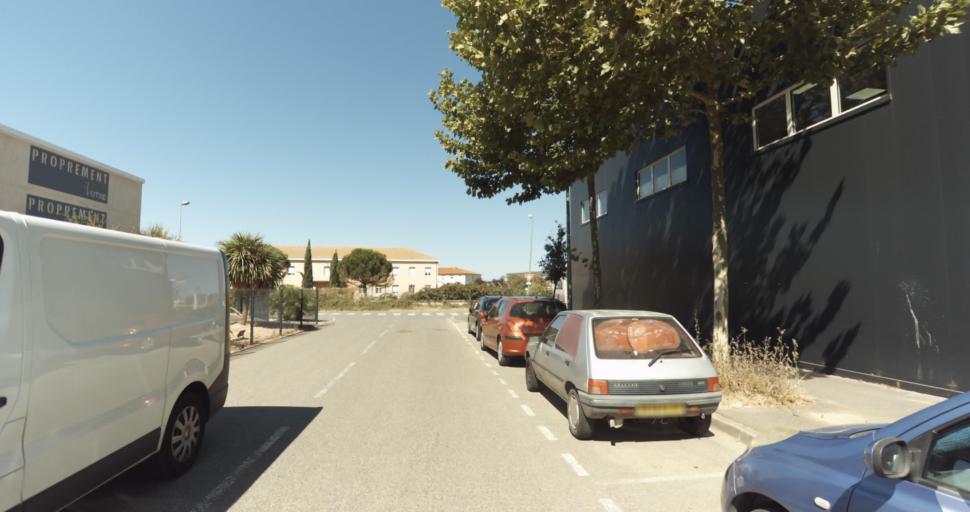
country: FR
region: Midi-Pyrenees
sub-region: Departement de la Haute-Garonne
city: L'Union
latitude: 43.6380
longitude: 1.4938
